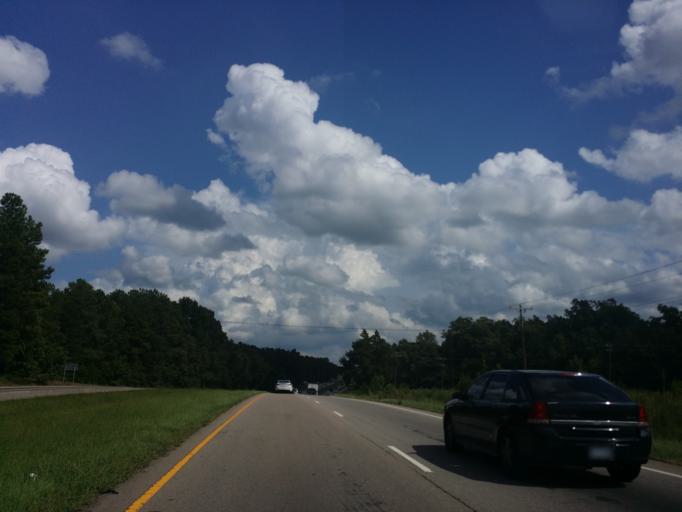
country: US
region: North Carolina
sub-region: Durham County
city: Durham
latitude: 35.9397
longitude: -78.8202
